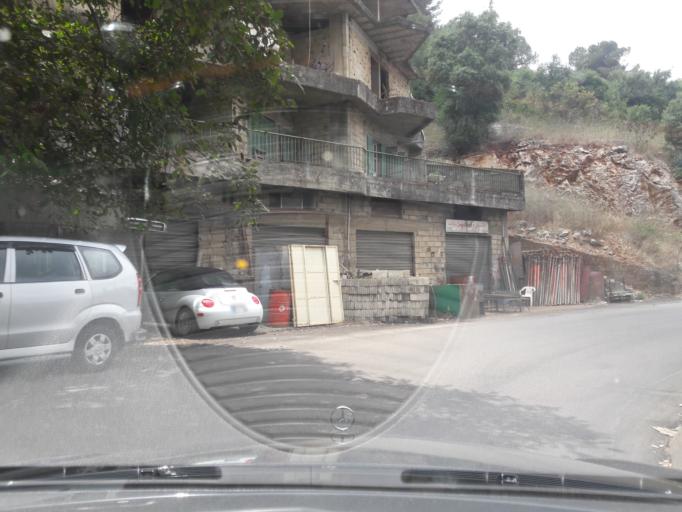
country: LB
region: Mont-Liban
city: Djounie
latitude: 33.9230
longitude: 35.6719
